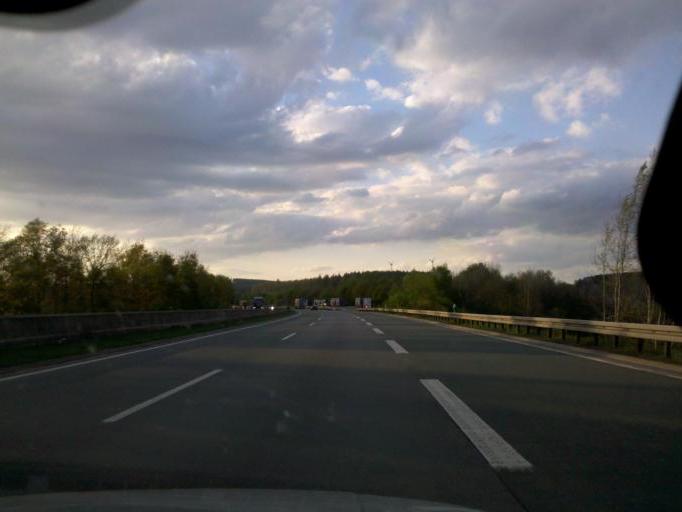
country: DE
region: North Rhine-Westphalia
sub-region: Regierungsbezirk Arnsberg
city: Wenden
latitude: 50.9420
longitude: 7.8779
